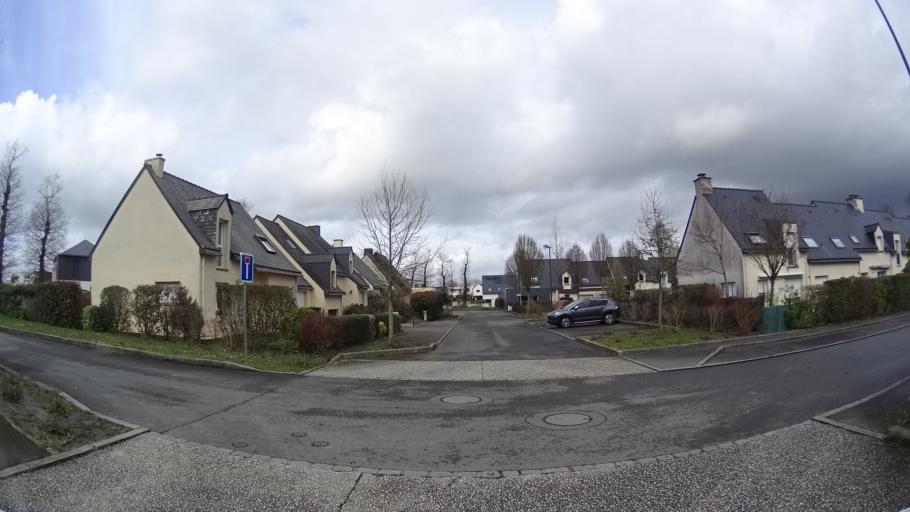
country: FR
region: Brittany
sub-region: Departement d'Ille-et-Vilaine
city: Saint-Gilles
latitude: 48.1497
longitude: -1.8363
